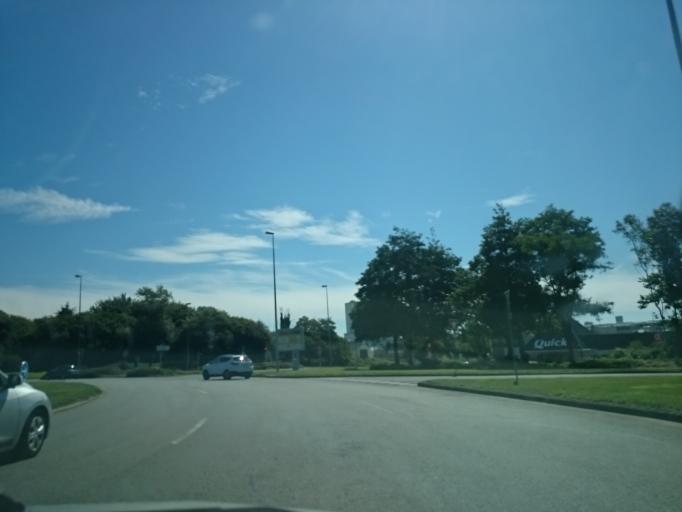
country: FR
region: Brittany
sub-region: Departement du Finistere
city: Brest
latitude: 48.4140
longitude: -4.4799
